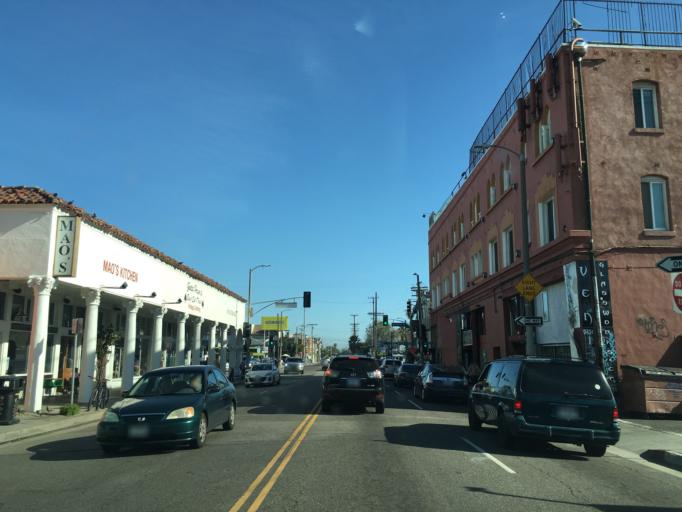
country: US
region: California
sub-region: Los Angeles County
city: Marina del Rey
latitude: 33.9882
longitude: -118.4727
